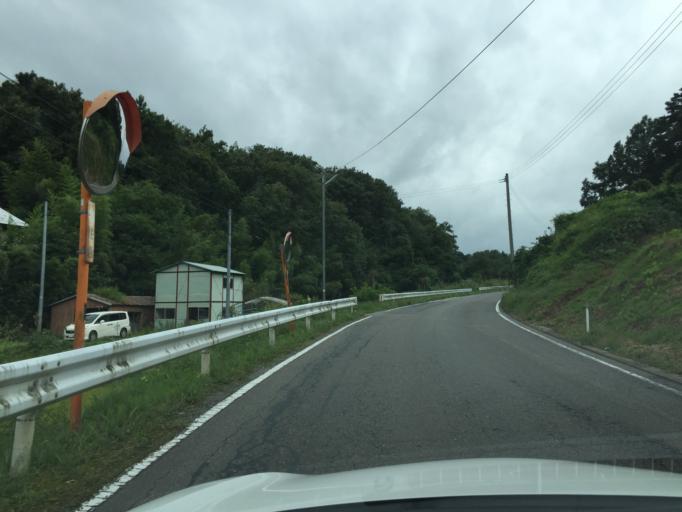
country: JP
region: Fukushima
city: Funehikimachi-funehiki
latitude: 37.4685
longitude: 140.5671
